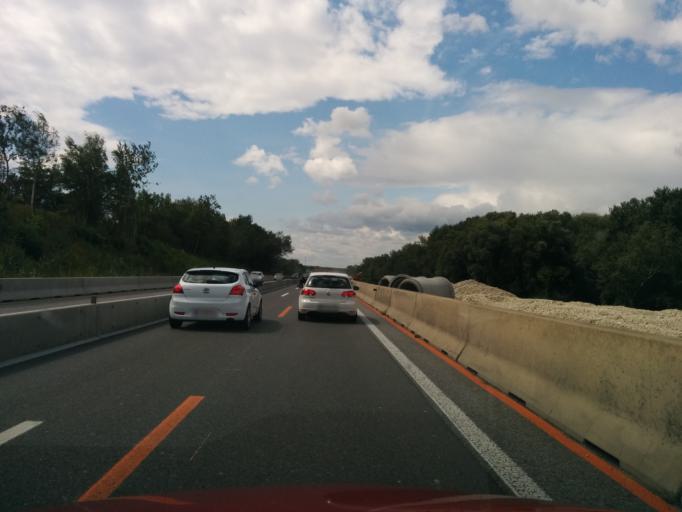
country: AT
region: Lower Austria
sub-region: Politischer Bezirk Wien-Umgebung
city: Fischamend Dorf
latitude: 48.1283
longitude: 16.5728
